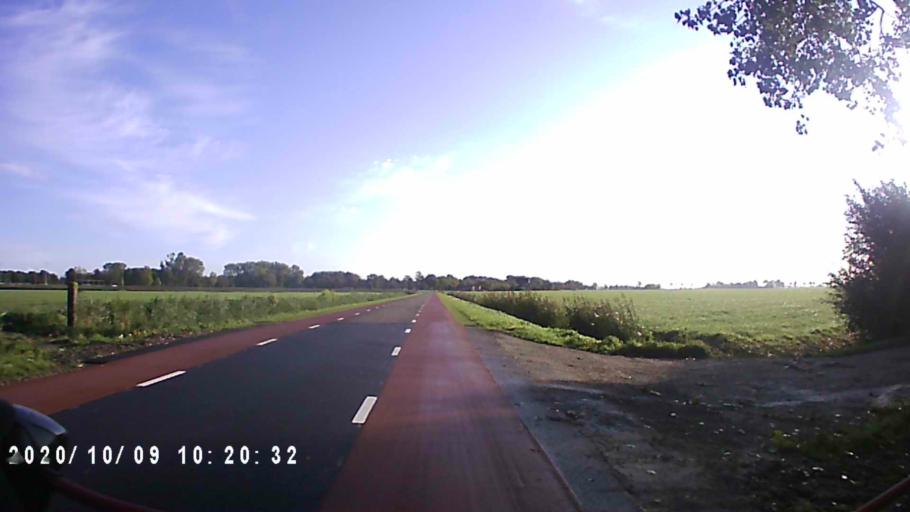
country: NL
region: Groningen
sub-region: Gemeente Winsum
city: Winsum
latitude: 53.3219
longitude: 6.5075
